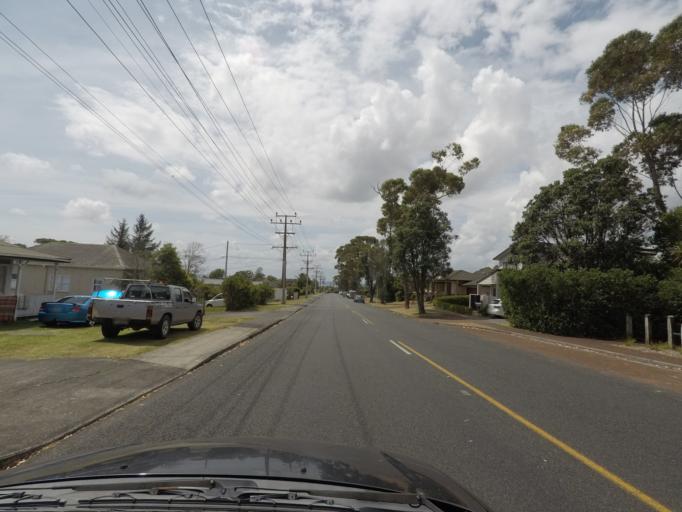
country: NZ
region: Auckland
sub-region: Auckland
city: Waitakere
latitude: -36.9004
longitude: 174.6422
